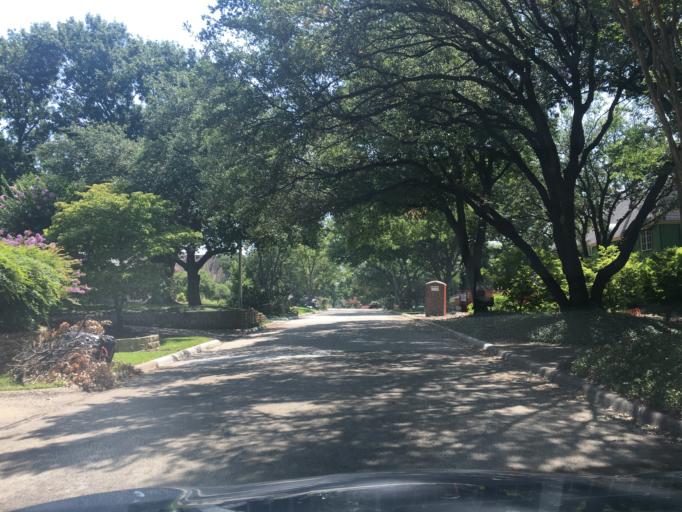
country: US
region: Texas
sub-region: Dallas County
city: Addison
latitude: 32.9116
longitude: -96.7944
